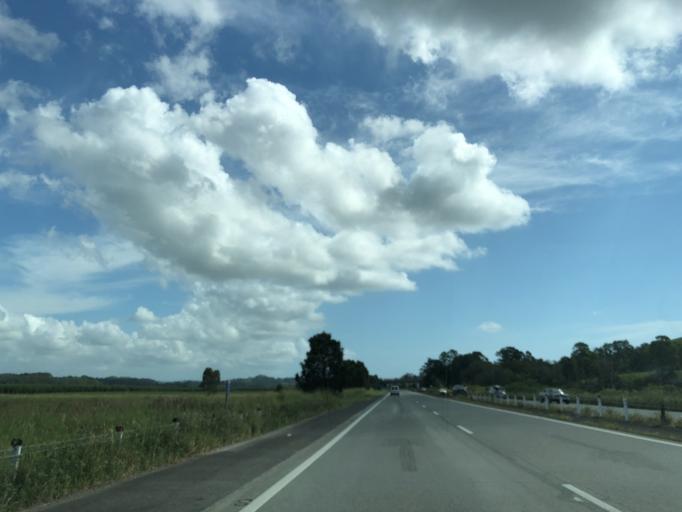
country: AU
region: New South Wales
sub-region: Tweed
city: Pottsville Beach
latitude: -28.3538
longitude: 153.5232
